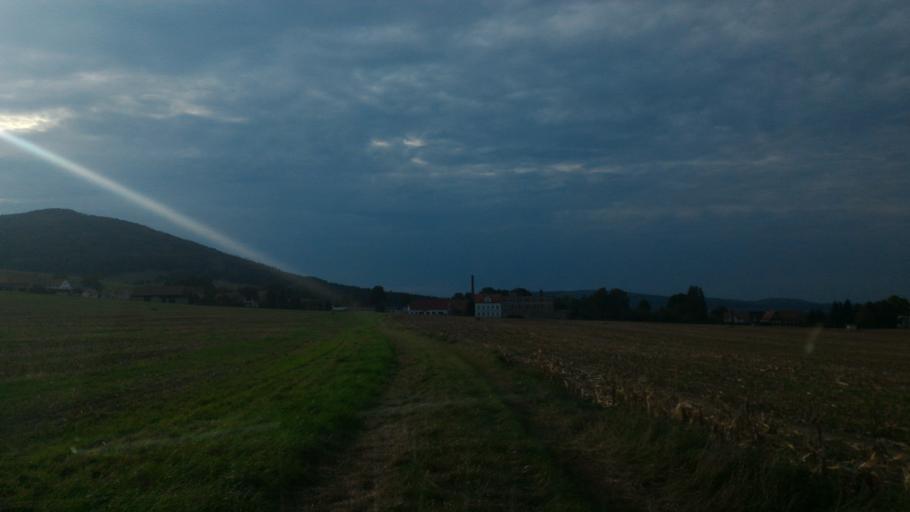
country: DE
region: Saxony
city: Grossschonau
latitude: 50.8707
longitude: 14.6589
